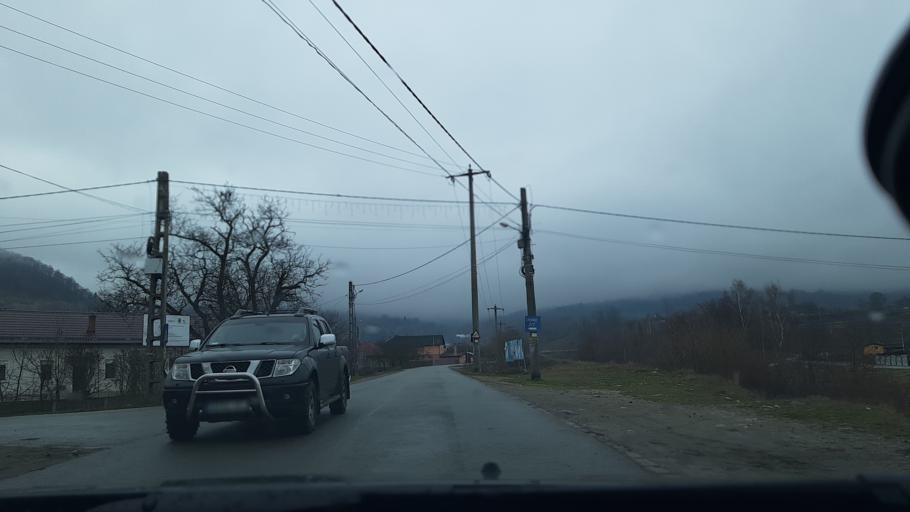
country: RO
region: Hunedoara
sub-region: Oras Petrila
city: Petrila
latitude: 45.4256
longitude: 23.4237
